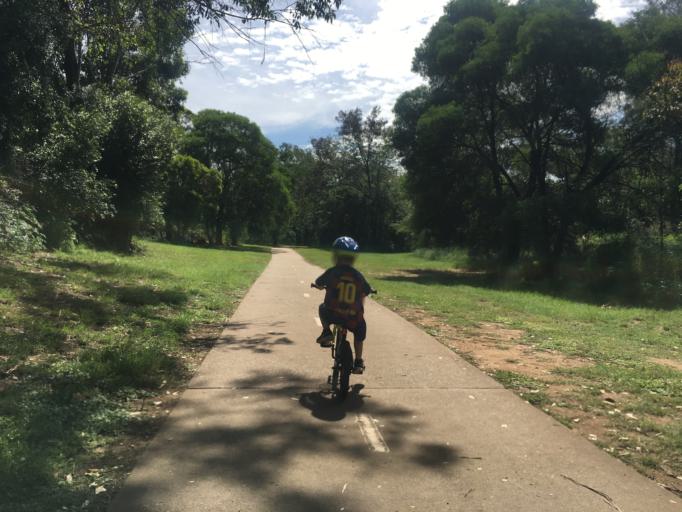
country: AU
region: New South Wales
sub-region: Camden
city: Camden South
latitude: -34.0745
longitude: 150.7004
